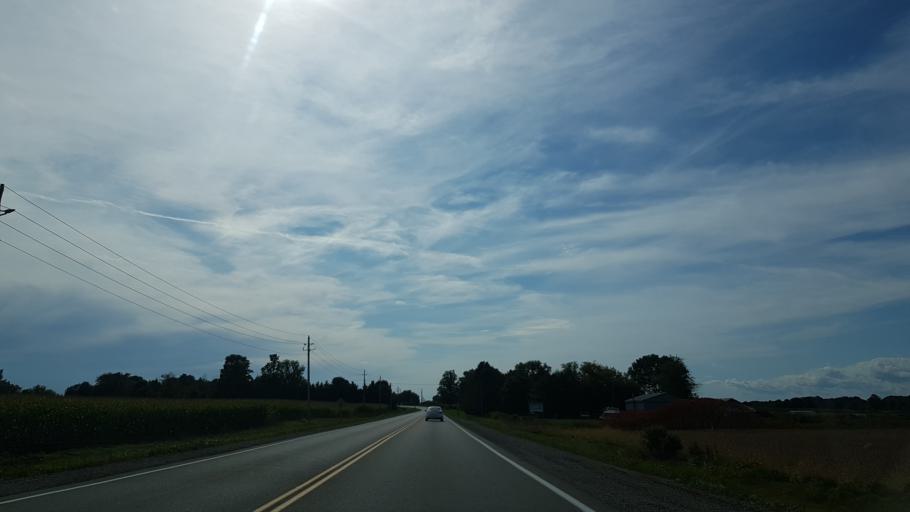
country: CA
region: Ontario
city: Delaware
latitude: 42.9767
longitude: -81.3884
